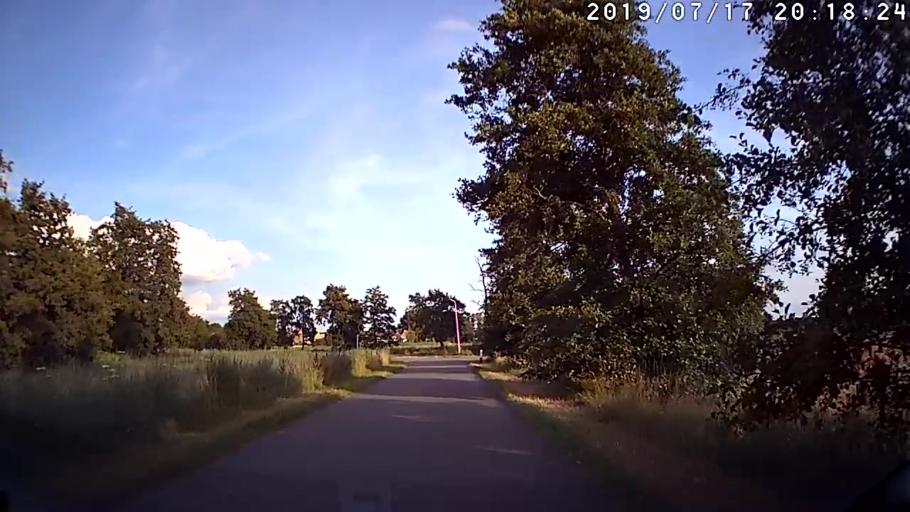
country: NL
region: Overijssel
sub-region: Gemeente Zwolle
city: Zwolle
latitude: 52.5431
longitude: 6.0908
